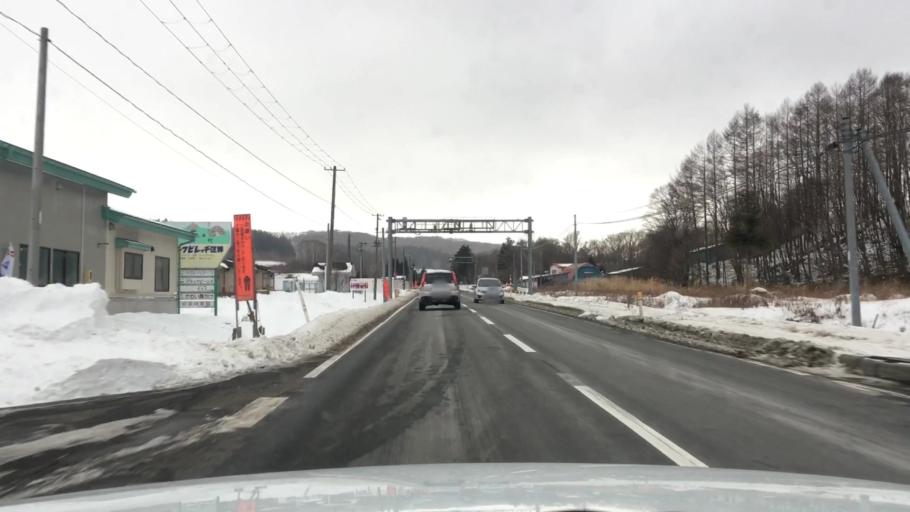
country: JP
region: Iwate
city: Morioka-shi
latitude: 39.6456
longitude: 141.3666
